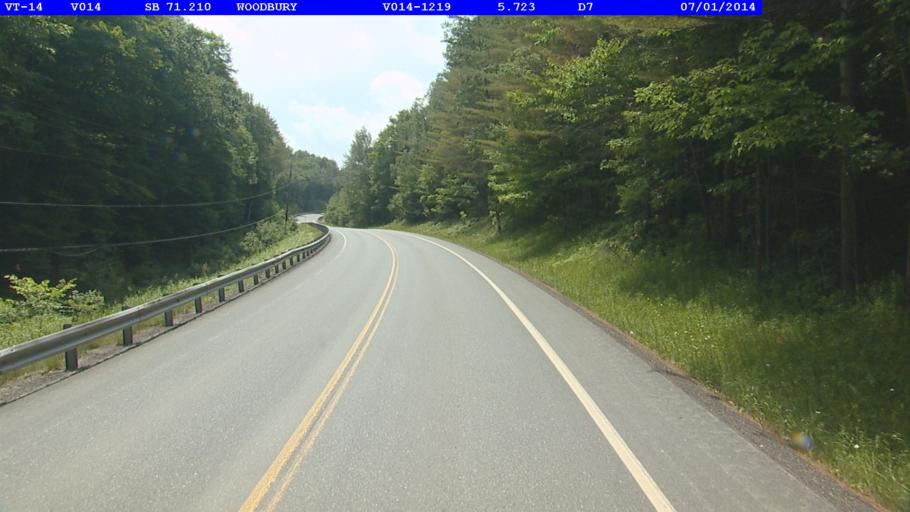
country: US
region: Vermont
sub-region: Caledonia County
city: Hardwick
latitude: 44.4673
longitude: -72.4100
